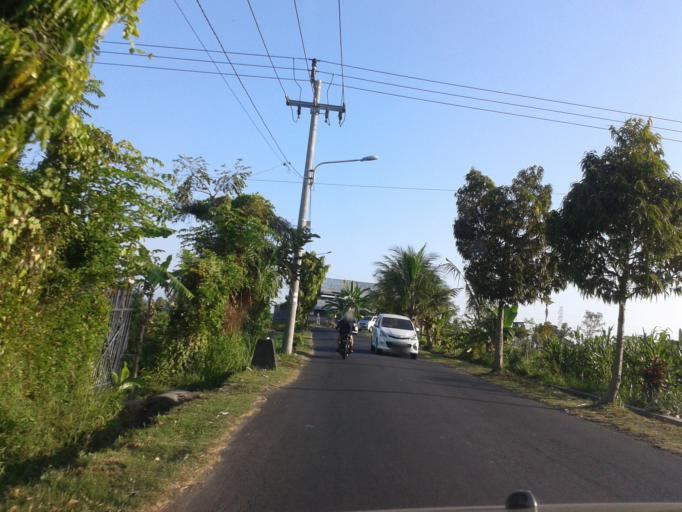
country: ID
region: Bali
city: Semarapura
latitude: -8.5584
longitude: 115.3871
